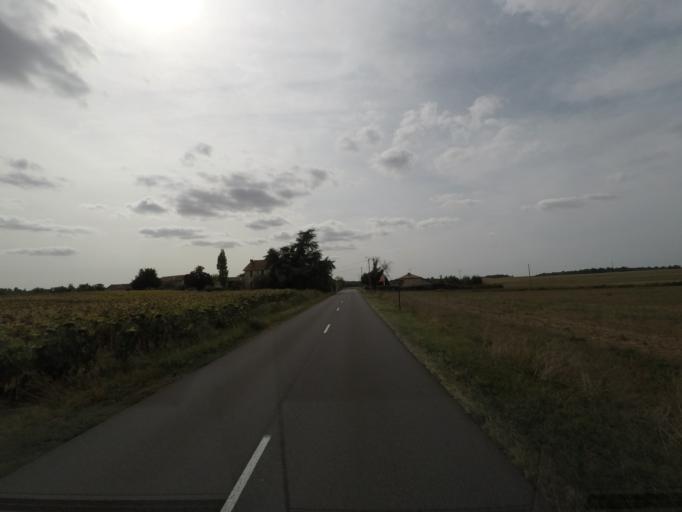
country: FR
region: Poitou-Charentes
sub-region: Departement de la Charente
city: Nanteuil-en-Vallee
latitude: 46.0185
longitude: 0.2807
